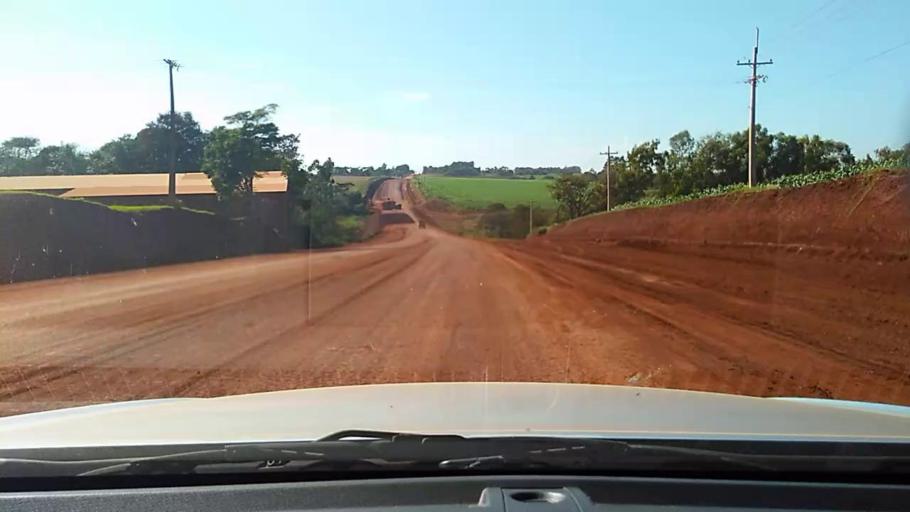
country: PY
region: Alto Parana
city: Naranjal
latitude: -25.9230
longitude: -55.4083
